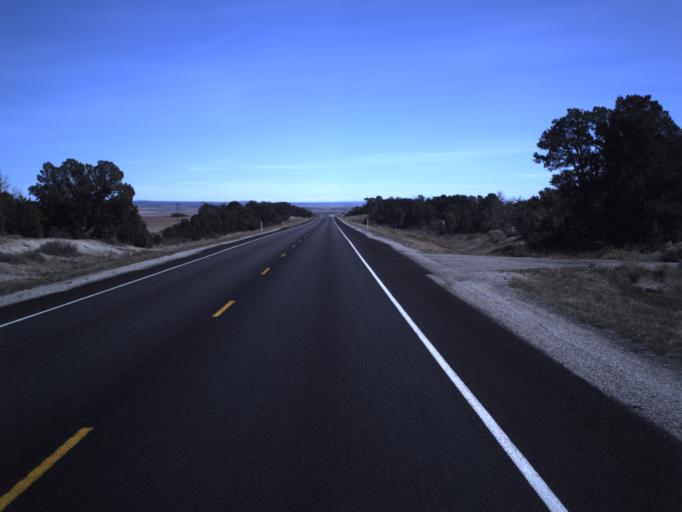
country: US
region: Colorado
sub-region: Dolores County
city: Dove Creek
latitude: 37.8259
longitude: -109.0747
